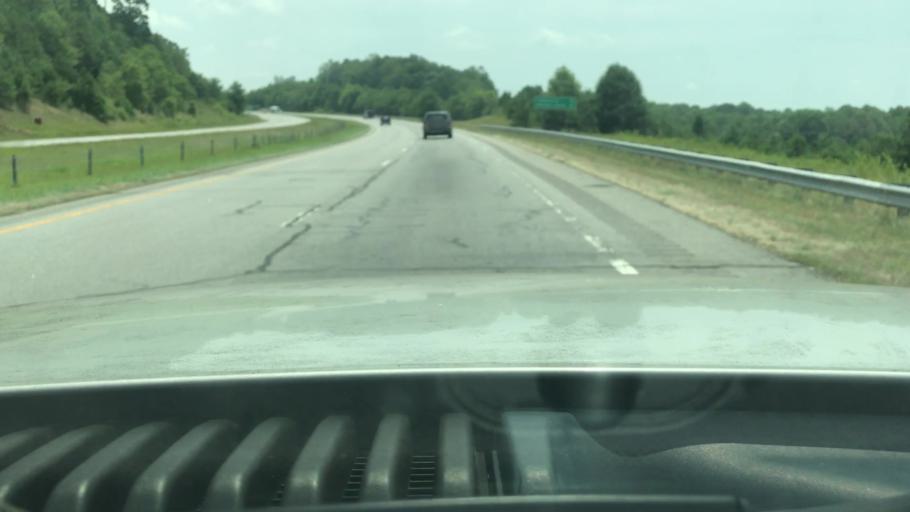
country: US
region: North Carolina
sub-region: Yadkin County
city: Jonesville
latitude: 36.1476
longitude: -80.9169
